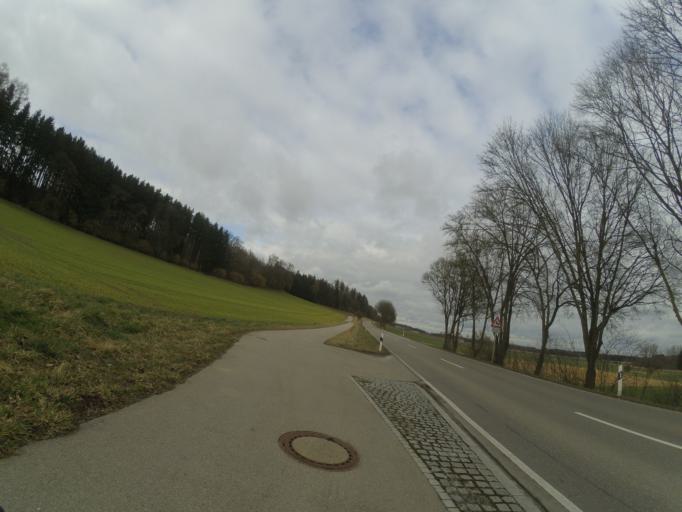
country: DE
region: Bavaria
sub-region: Swabia
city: Bellenberg
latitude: 48.2592
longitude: 10.1272
